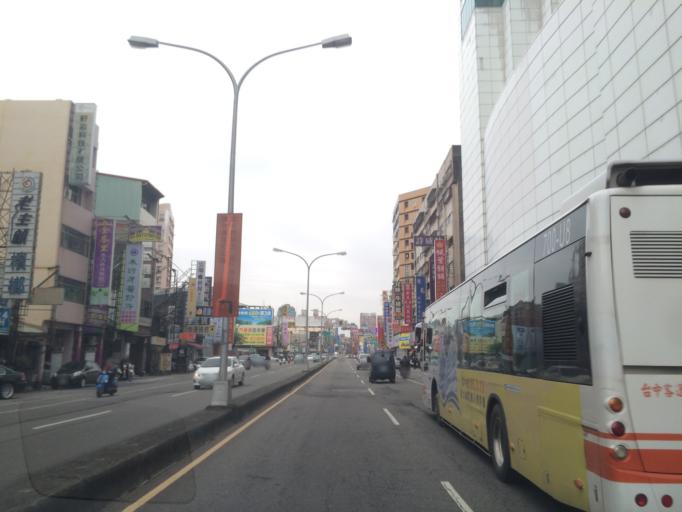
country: TW
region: Taiwan
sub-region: Taichung City
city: Taichung
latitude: 24.1605
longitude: 120.6920
